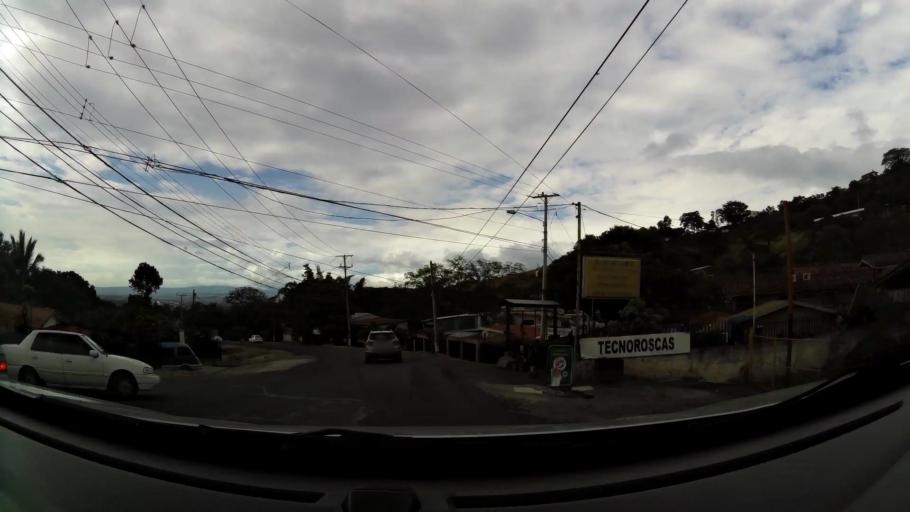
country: CR
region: San Jose
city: Santa Ana
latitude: 9.9289
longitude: -84.1736
